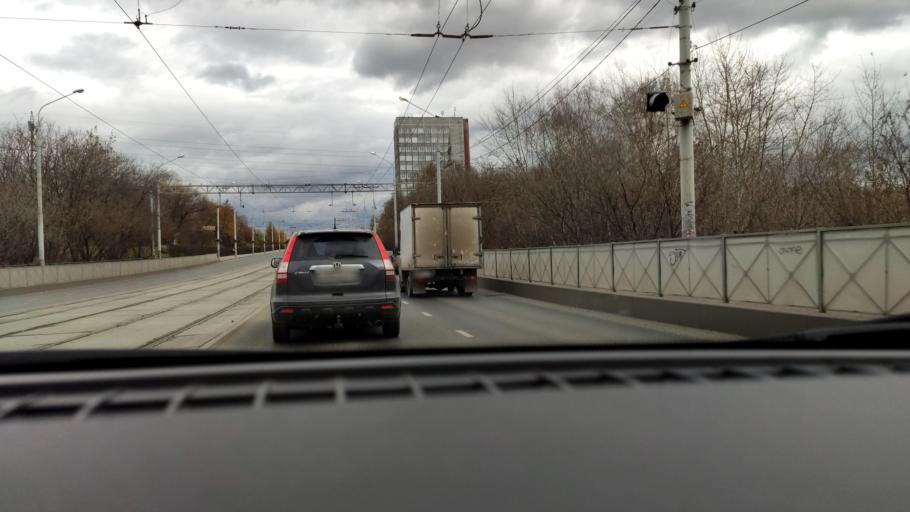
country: RU
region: Perm
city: Perm
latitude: 58.0169
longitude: 56.2685
